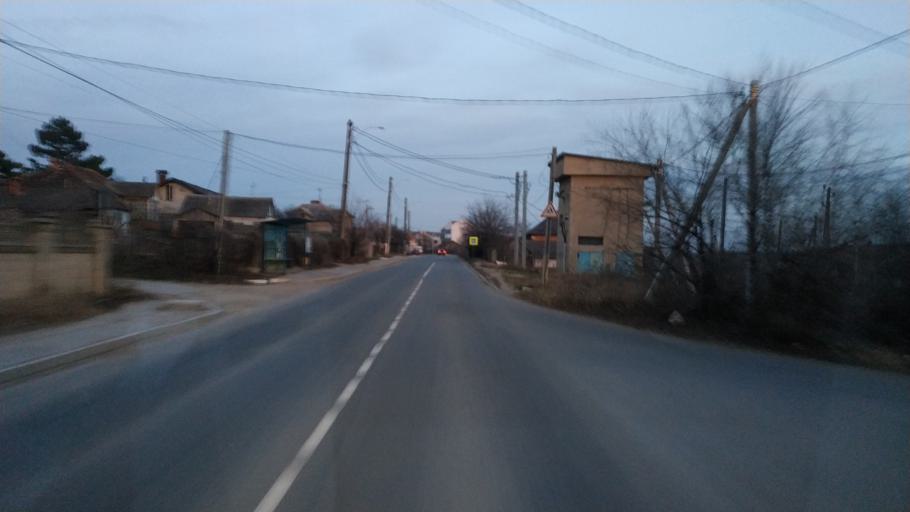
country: MD
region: Laloveni
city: Ialoveni
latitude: 46.9409
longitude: 28.7862
